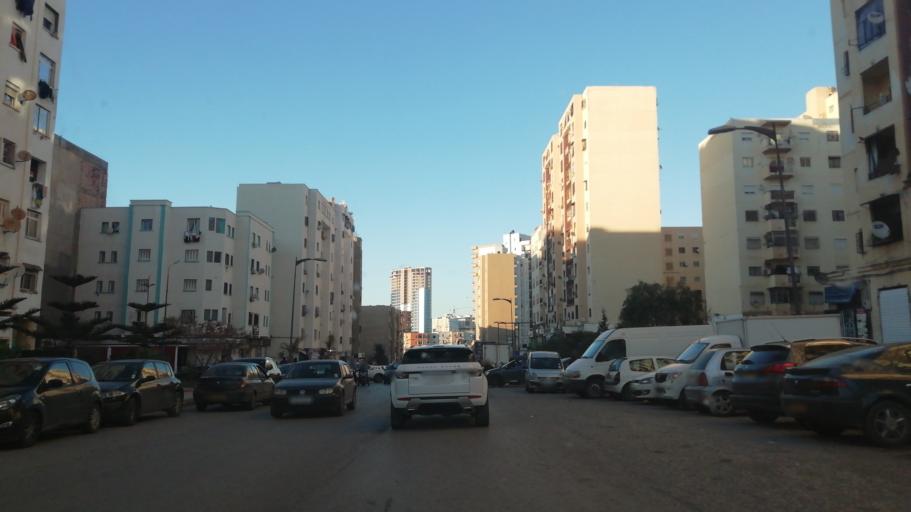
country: DZ
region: Oran
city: Bir el Djir
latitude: 35.7213
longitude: -0.5879
